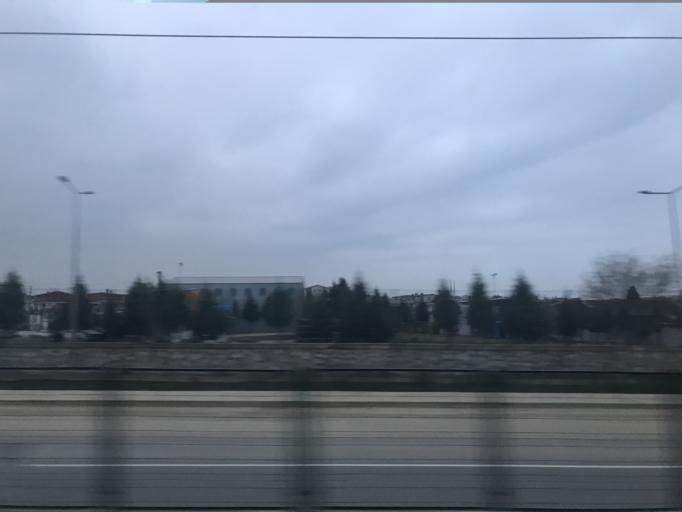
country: TR
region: Kocaeli
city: Darica
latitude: 40.7943
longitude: 29.3873
